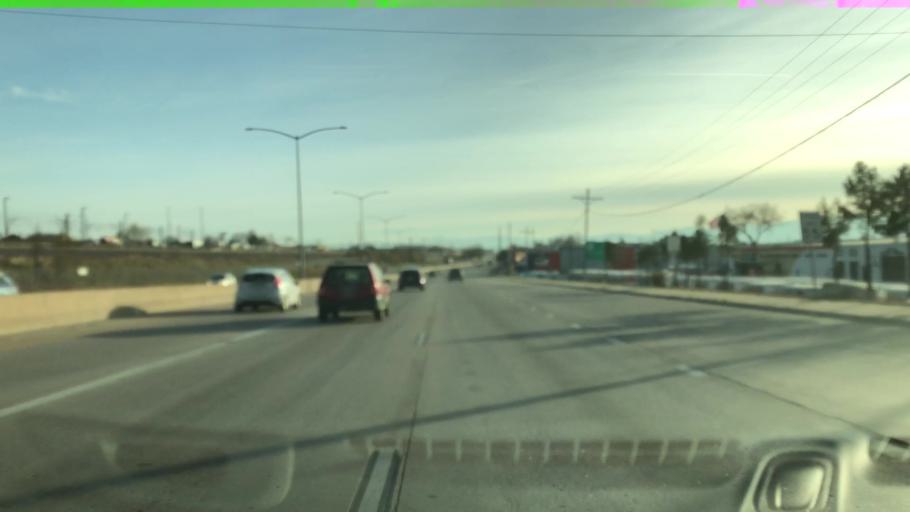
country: US
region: Colorado
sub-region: Arapahoe County
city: Englewood
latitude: 39.6668
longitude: -104.9965
